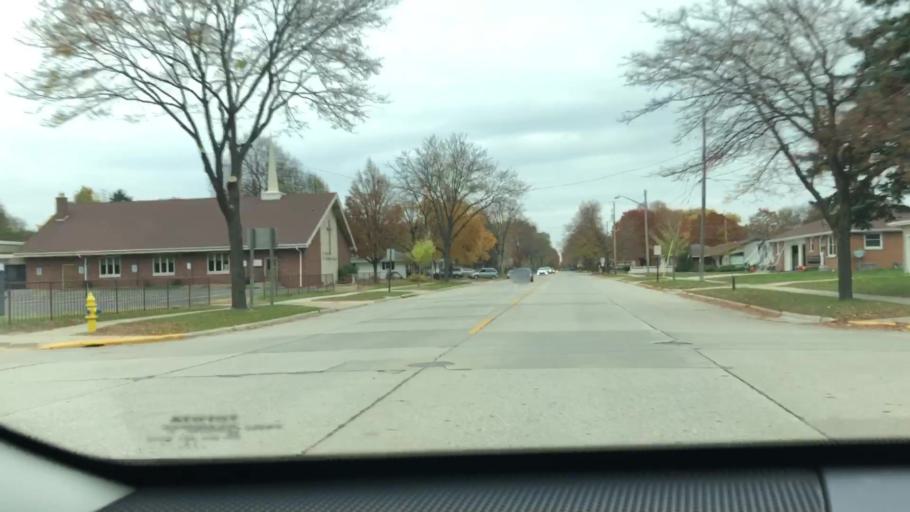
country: US
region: Wisconsin
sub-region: Brown County
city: Ashwaubenon
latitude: 44.5028
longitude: -88.0560
